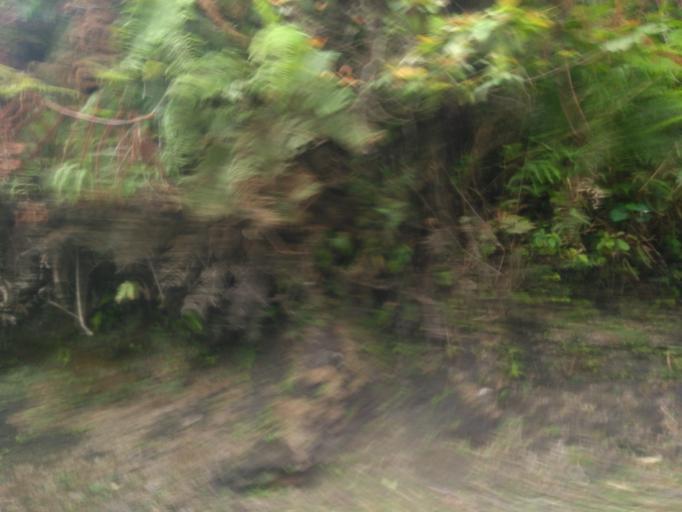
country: MY
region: Pahang
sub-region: Cameron Highlands
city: Tanah Rata
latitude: 4.4651
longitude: 101.3680
